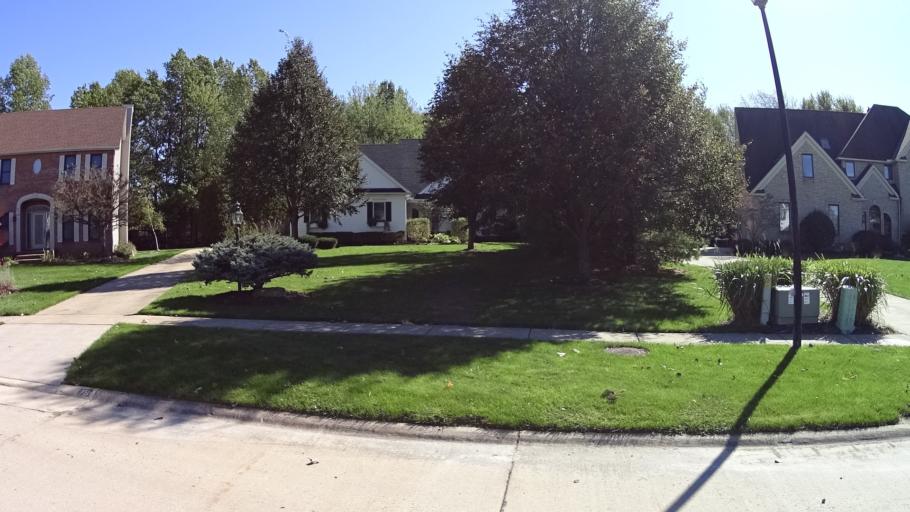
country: US
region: Ohio
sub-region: Lorain County
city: Amherst
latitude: 41.3841
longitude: -82.2257
